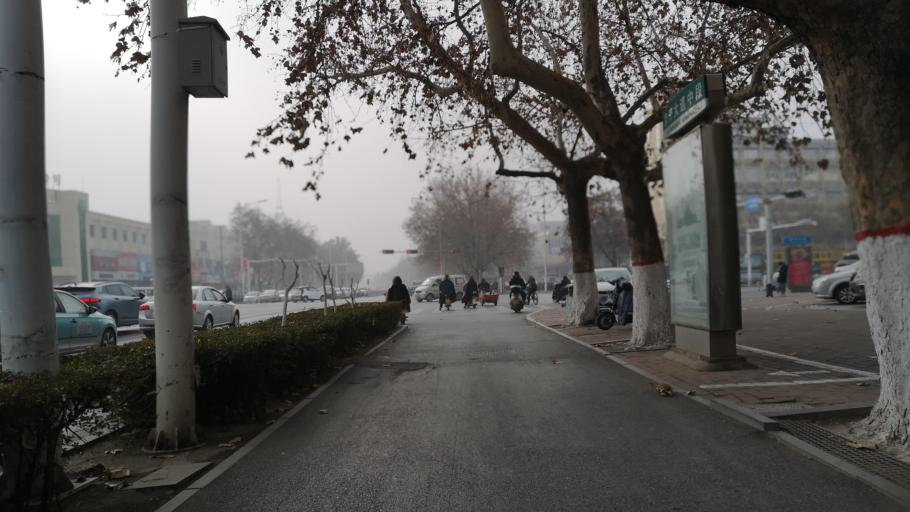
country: CN
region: Henan Sheng
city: Zhongyuanlu
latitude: 35.7725
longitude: 115.0393
